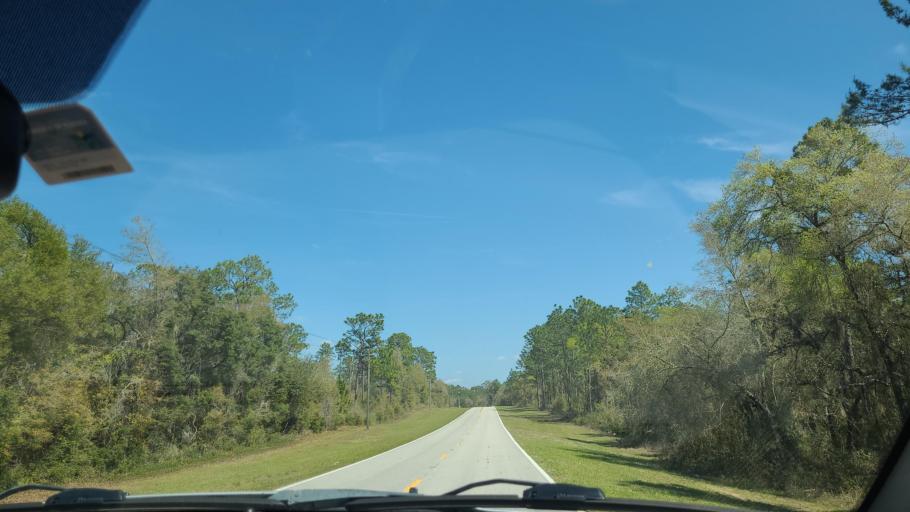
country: US
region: Florida
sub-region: Putnam County
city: Interlachen
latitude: 29.3663
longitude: -81.8141
